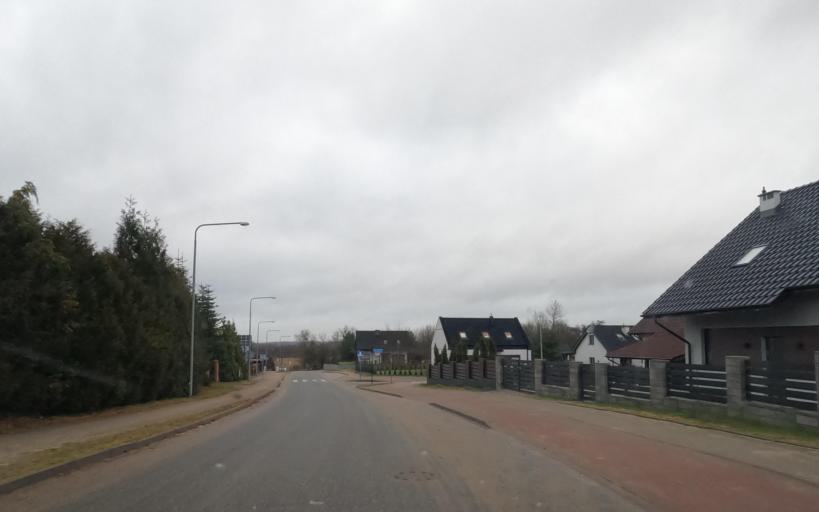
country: PL
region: West Pomeranian Voivodeship
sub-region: Powiat szczecinecki
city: Szczecinek
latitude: 53.7133
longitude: 16.7323
